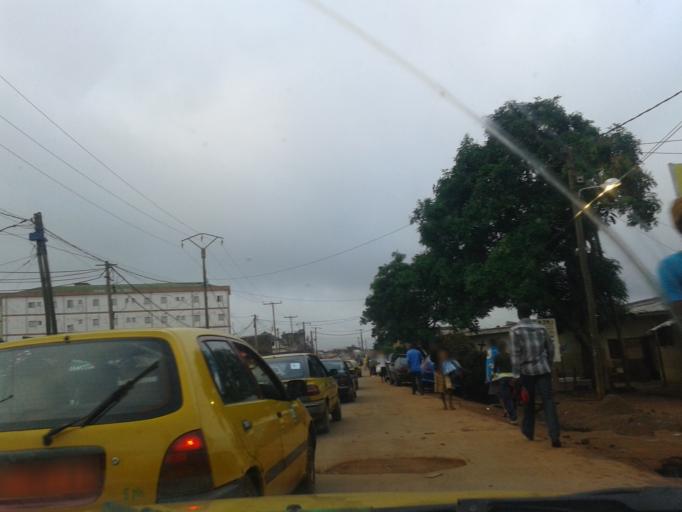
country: CM
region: Centre
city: Yaounde
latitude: 3.8929
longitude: 11.5296
